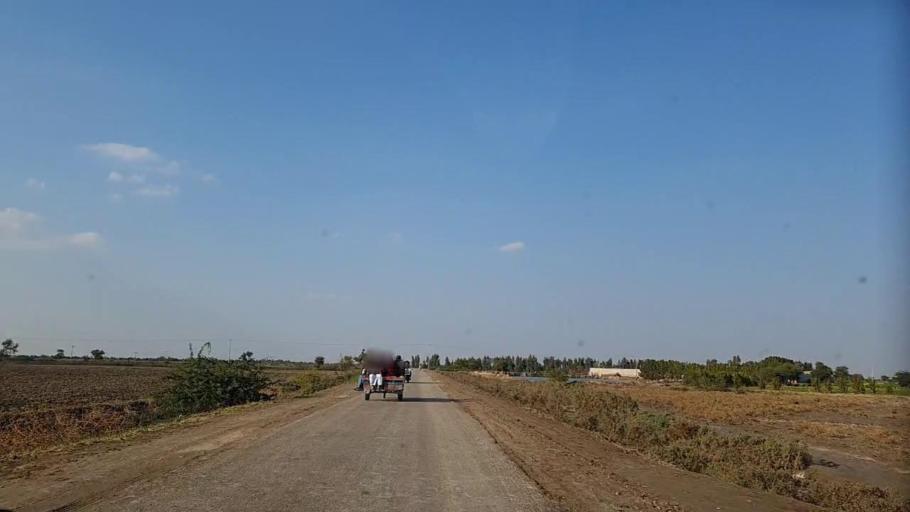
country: PK
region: Sindh
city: Pithoro
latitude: 25.7111
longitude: 69.2208
